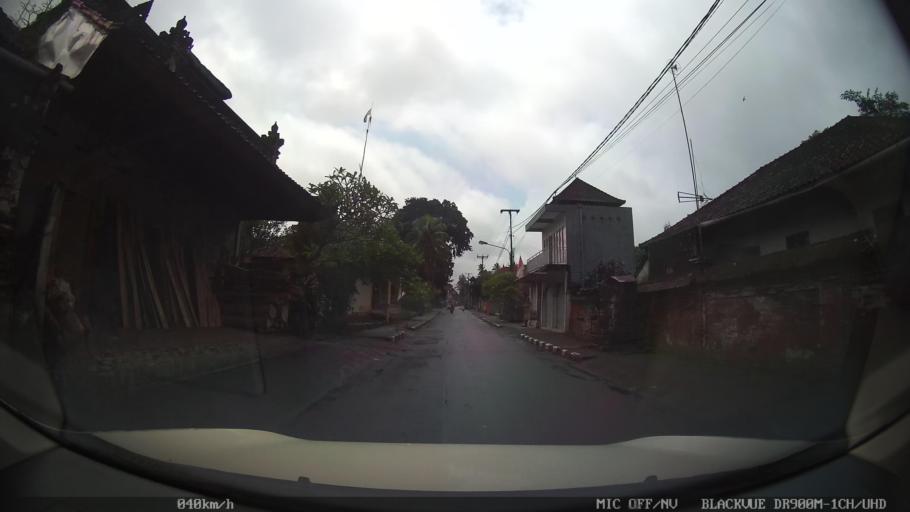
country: ID
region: Bali
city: Pegongan
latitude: -8.4892
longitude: 115.2263
